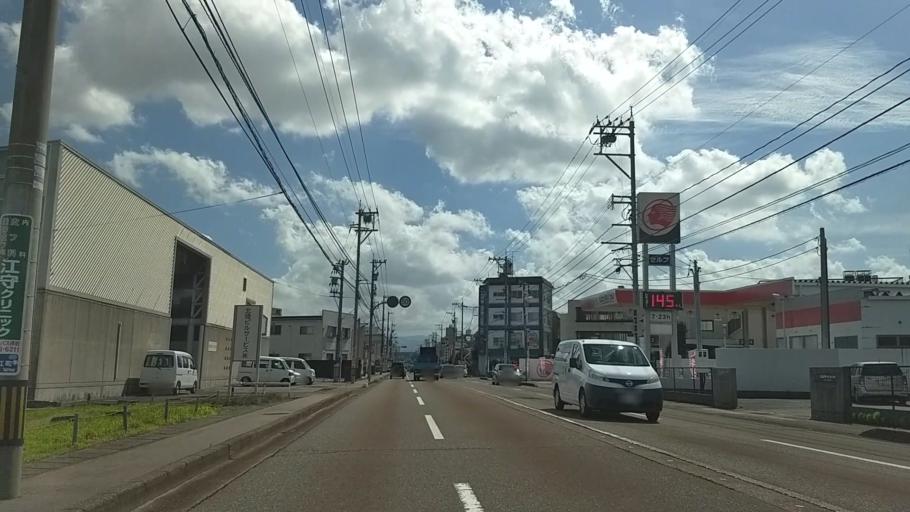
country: JP
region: Ishikawa
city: Kanazawa-shi
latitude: 36.6037
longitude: 136.6357
